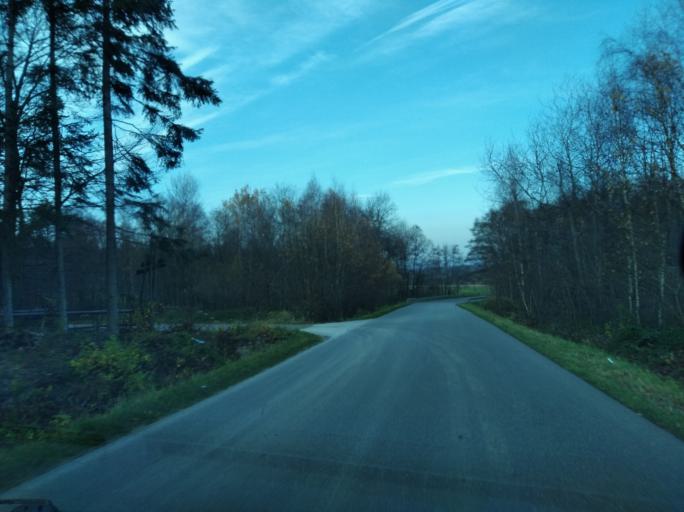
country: PL
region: Subcarpathian Voivodeship
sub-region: Powiat ropczycko-sedziszowski
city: Zagorzyce
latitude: 49.9671
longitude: 21.6962
